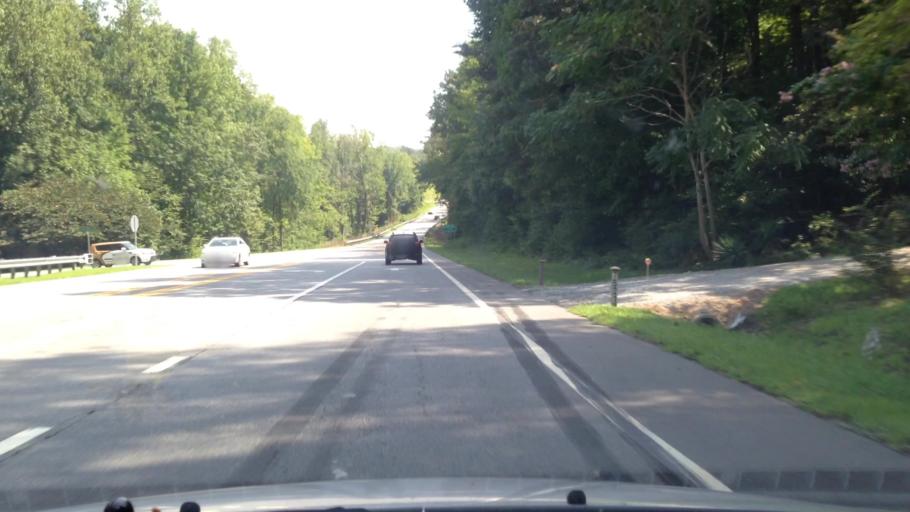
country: US
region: North Carolina
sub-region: Guilford County
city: Oak Ridge
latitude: 36.2010
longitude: -79.9859
